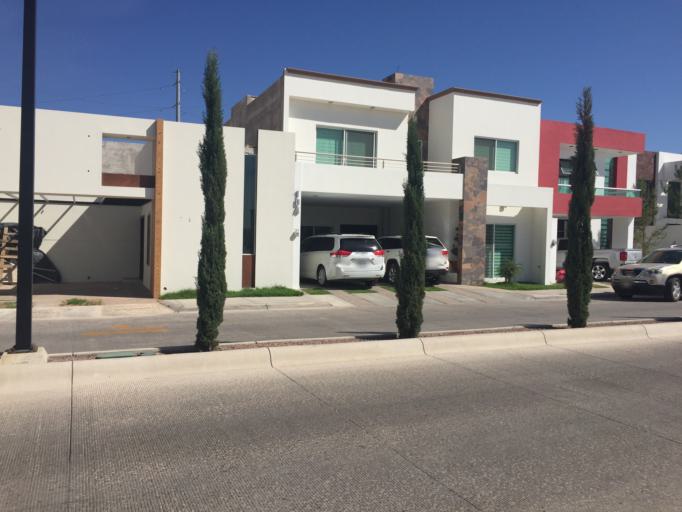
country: MX
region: Durango
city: Victoria de Durango
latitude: 23.9999
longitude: -104.6388
